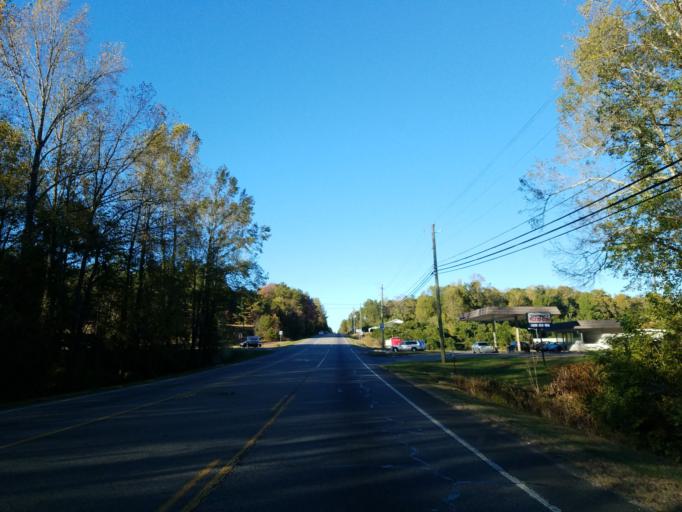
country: US
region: Georgia
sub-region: Cherokee County
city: Ball Ground
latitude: 34.3471
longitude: -84.3800
